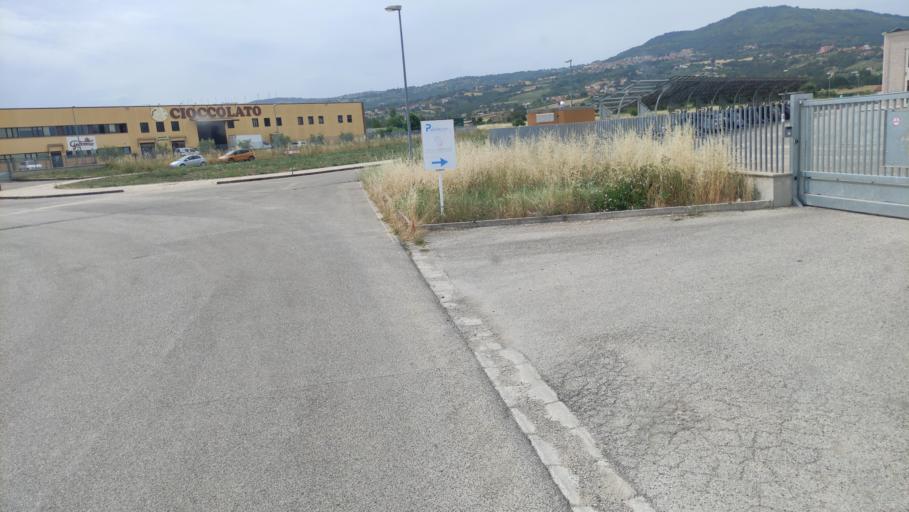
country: IT
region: Campania
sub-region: Provincia di Avellino
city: Sturno
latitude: 41.0493
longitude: 15.1220
